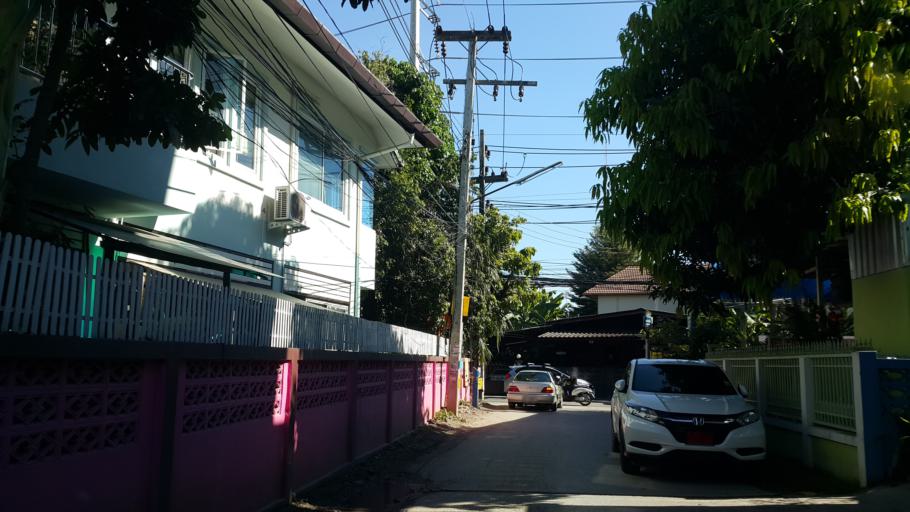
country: TH
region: Chiang Mai
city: Chiang Mai
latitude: 18.7620
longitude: 98.9984
